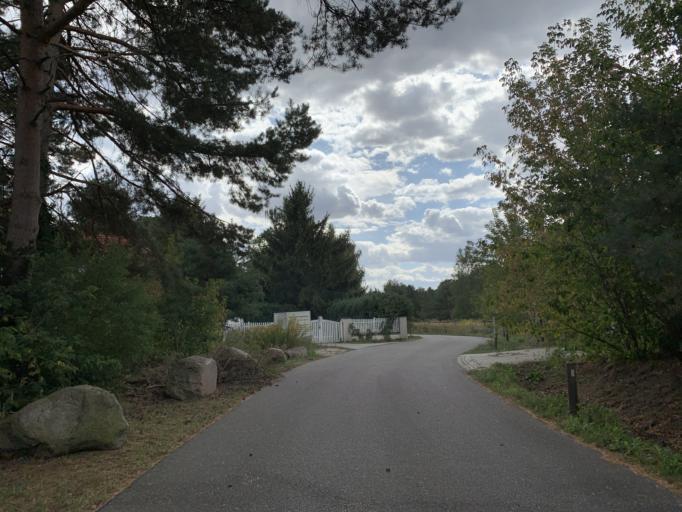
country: DE
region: Berlin
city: Wannsee
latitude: 52.4034
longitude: 13.1699
